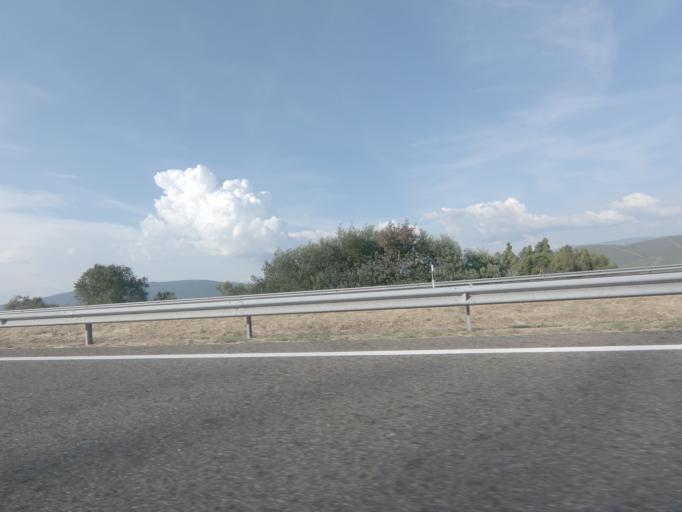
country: ES
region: Galicia
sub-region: Provincia de Ourense
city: Verin
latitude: 41.9586
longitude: -7.5133
